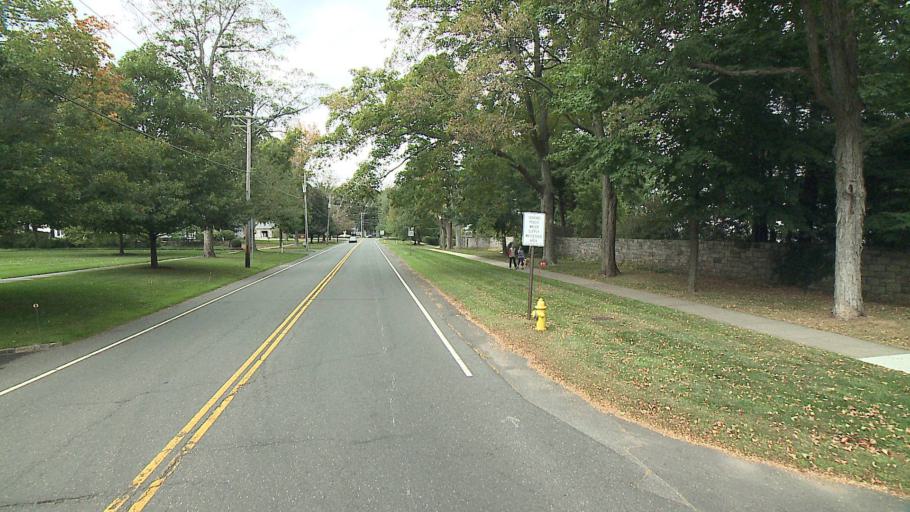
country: US
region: Connecticut
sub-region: Fairfield County
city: Ridgefield
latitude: 41.2709
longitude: -73.4962
